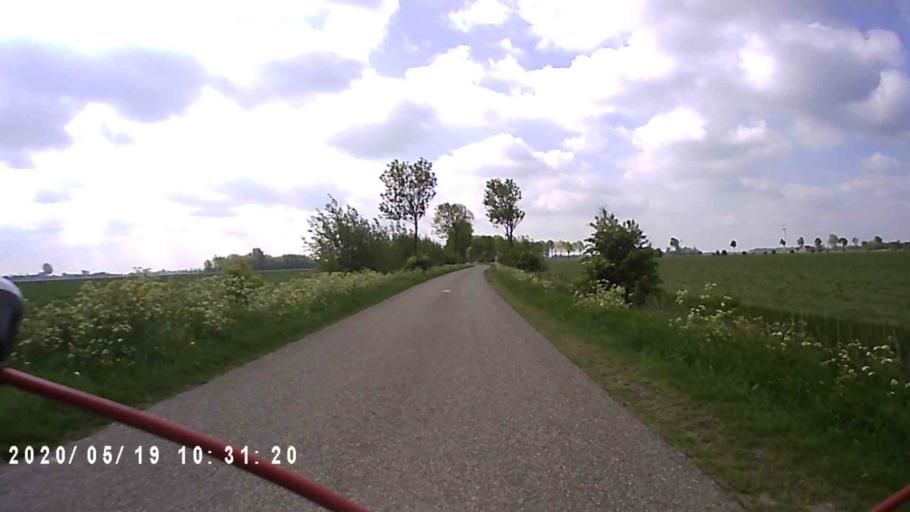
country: NL
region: Friesland
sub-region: Gemeente Kollumerland en Nieuwkruisland
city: Kollum
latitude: 53.2915
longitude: 6.1962
